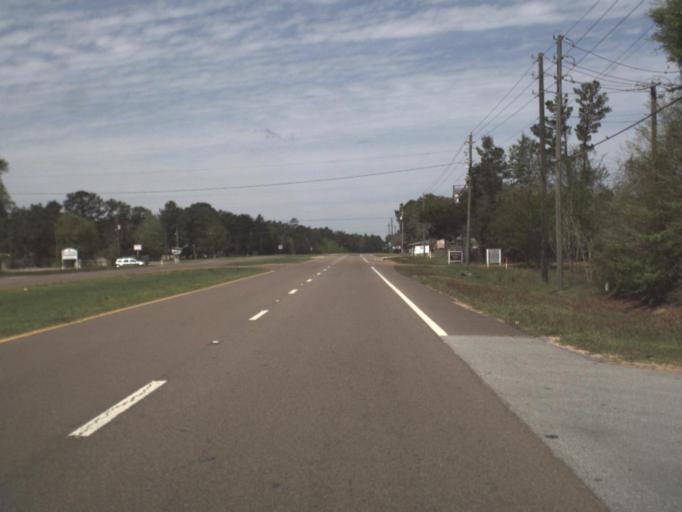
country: US
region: Florida
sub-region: Okaloosa County
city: Crestview
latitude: 30.7554
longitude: -86.5254
